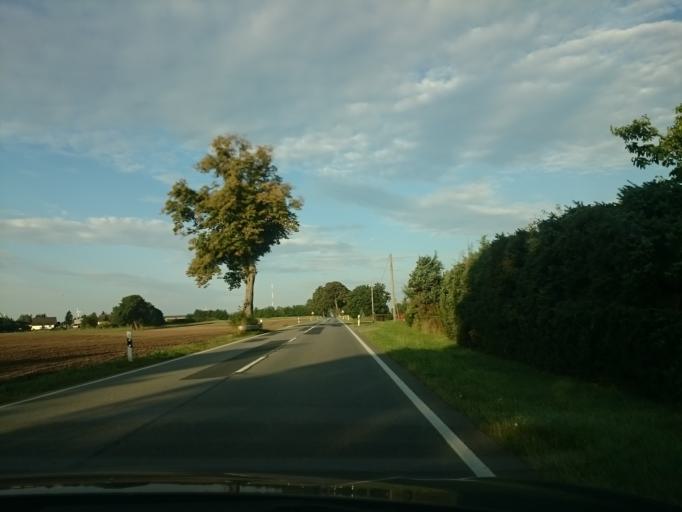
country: DE
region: Mecklenburg-Vorpommern
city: Zussow
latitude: 54.0050
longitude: 13.6218
